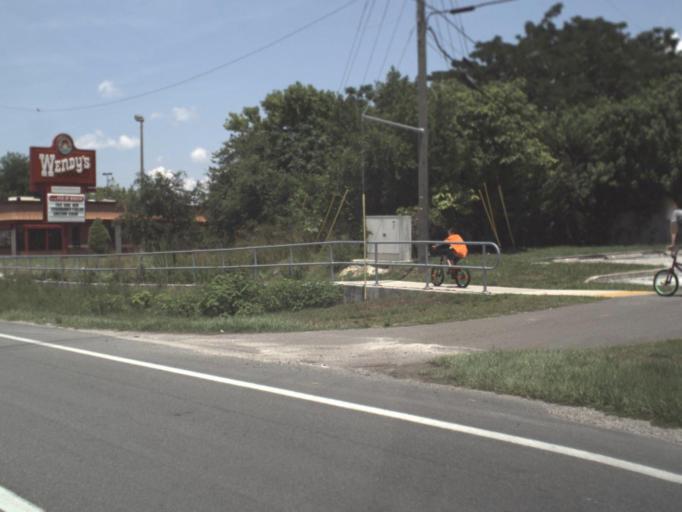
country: US
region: Florida
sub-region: Pasco County
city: Elfers
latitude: 28.2206
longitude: -82.7354
